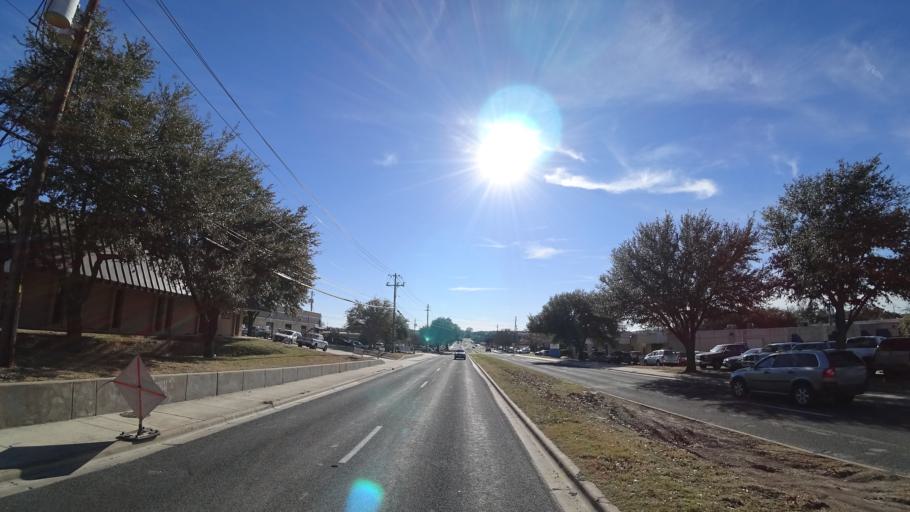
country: US
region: Texas
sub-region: Travis County
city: Wells Branch
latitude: 30.3859
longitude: -97.7120
